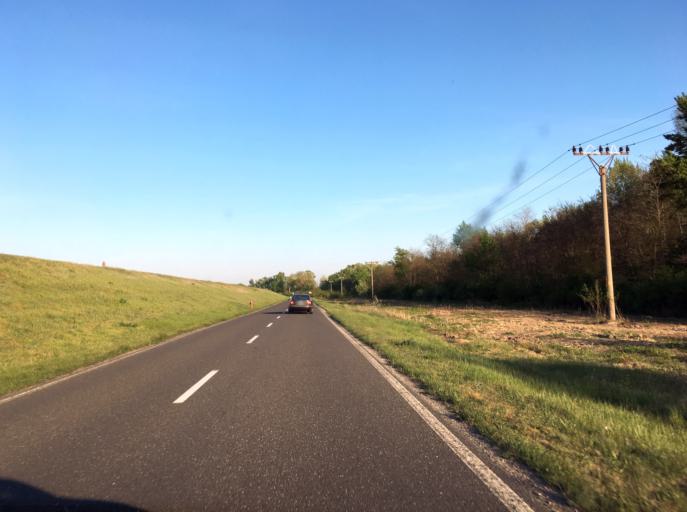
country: SK
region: Trnavsky
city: Samorin
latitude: 47.9990
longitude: 17.2663
